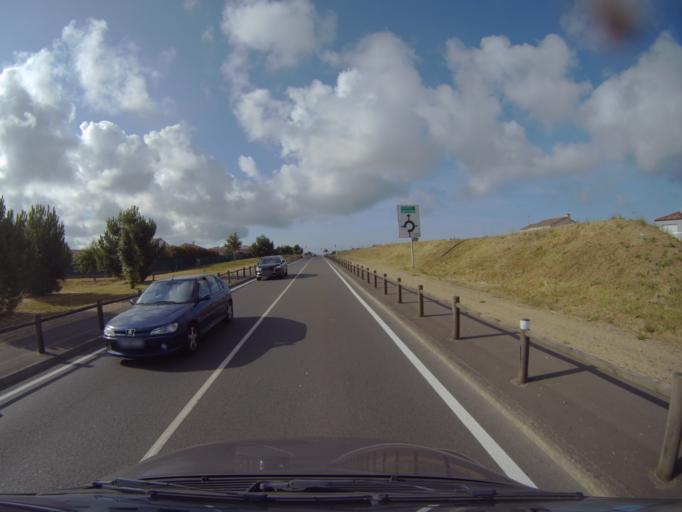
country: FR
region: Pays de la Loire
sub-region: Departement de la Vendee
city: Chateau-d'Olonne
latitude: 46.5094
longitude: -1.7572
